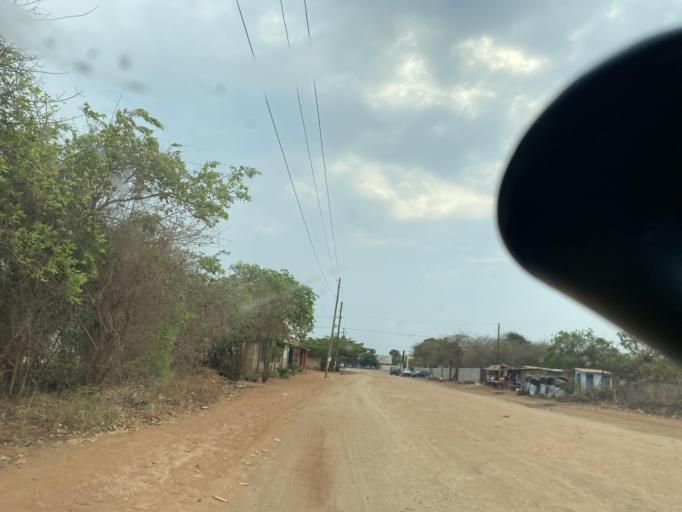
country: ZM
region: Lusaka
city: Lusaka
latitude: -15.2922
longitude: 28.2724
